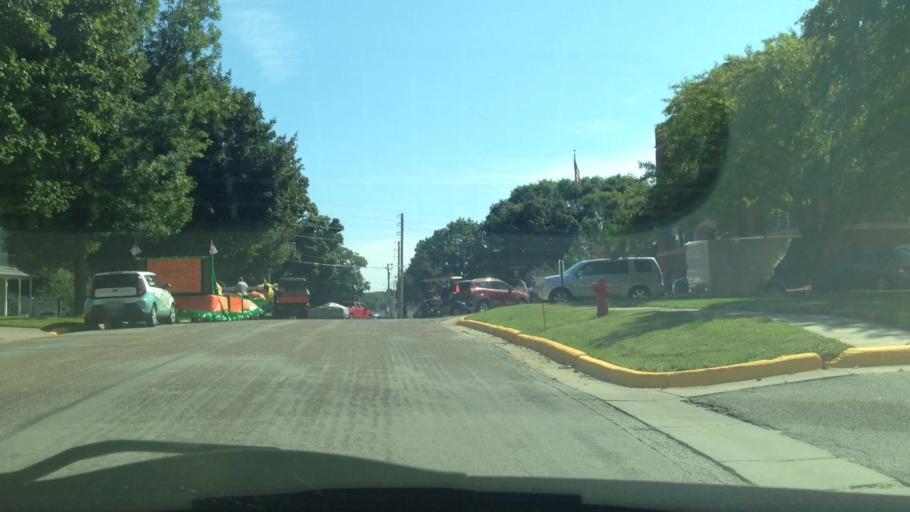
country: US
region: Minnesota
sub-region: Houston County
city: Spring Grove
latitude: 43.5205
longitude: -91.7740
